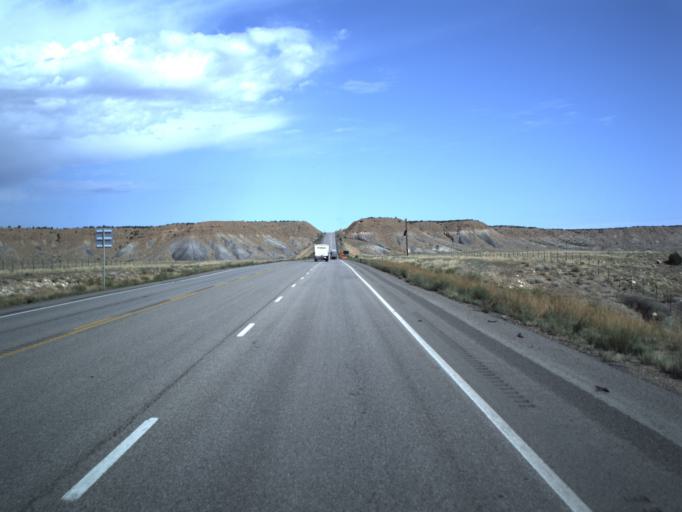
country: US
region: Utah
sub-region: Carbon County
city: East Carbon City
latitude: 39.3865
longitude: -110.4110
